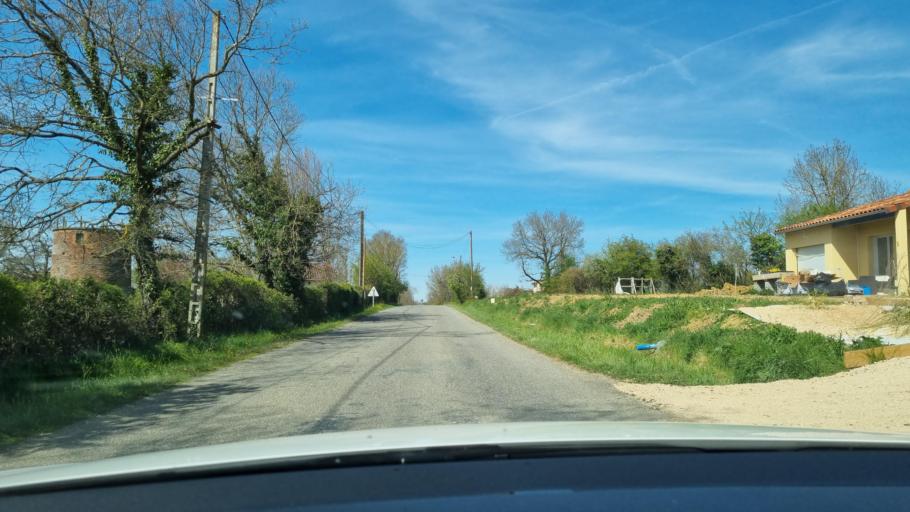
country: FR
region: Midi-Pyrenees
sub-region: Departement de la Haute-Garonne
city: Rieumes
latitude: 43.4682
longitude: 1.0627
